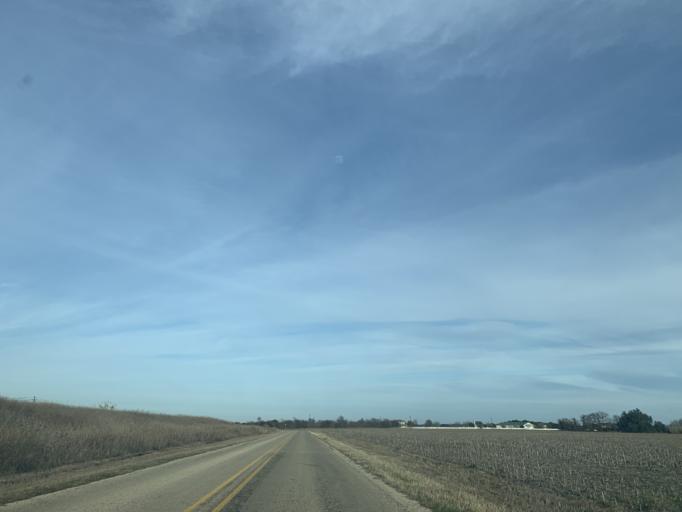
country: US
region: Texas
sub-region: Bell County
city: Salado
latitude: 30.9751
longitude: -97.5119
